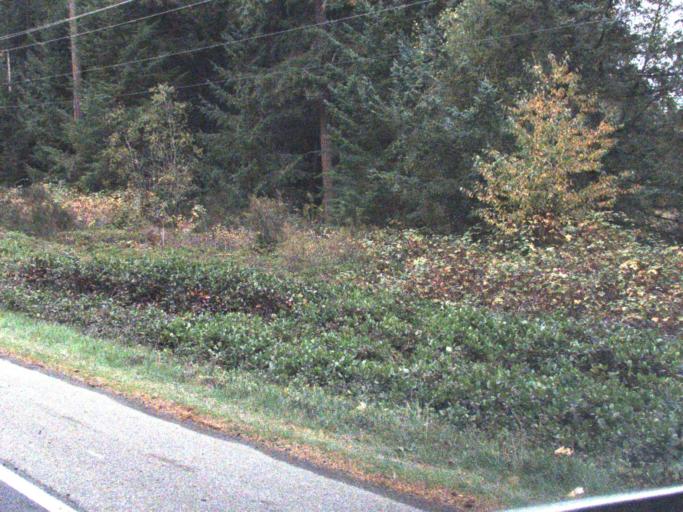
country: US
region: Washington
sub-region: Island County
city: Langley
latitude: 47.9845
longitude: -122.3895
